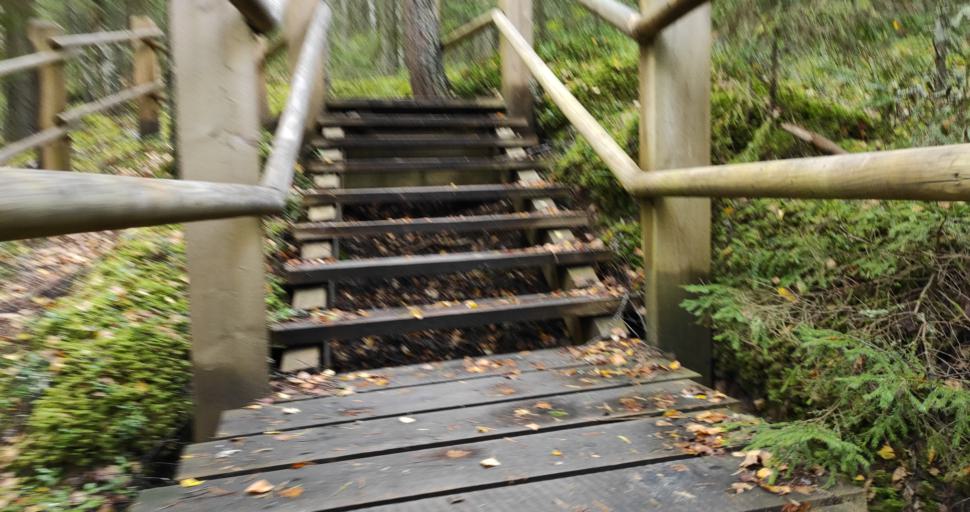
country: LV
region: Cesu Rajons
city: Cesis
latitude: 57.3597
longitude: 25.2536
